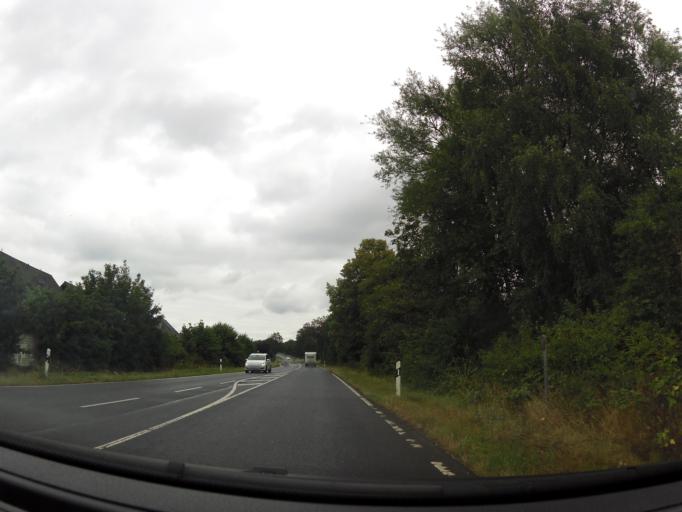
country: DE
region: North Rhine-Westphalia
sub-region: Regierungsbezirk Dusseldorf
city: Xanten
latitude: 51.6487
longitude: 6.4446
